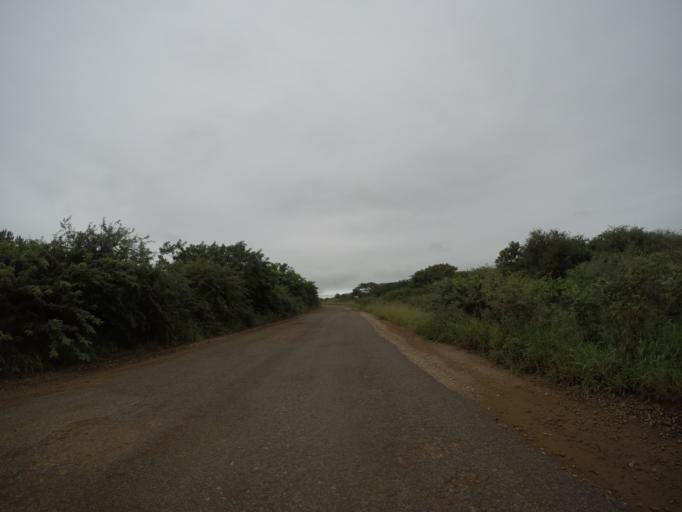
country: ZA
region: KwaZulu-Natal
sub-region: uThungulu District Municipality
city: Empangeni
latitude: -28.6587
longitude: 31.7859
